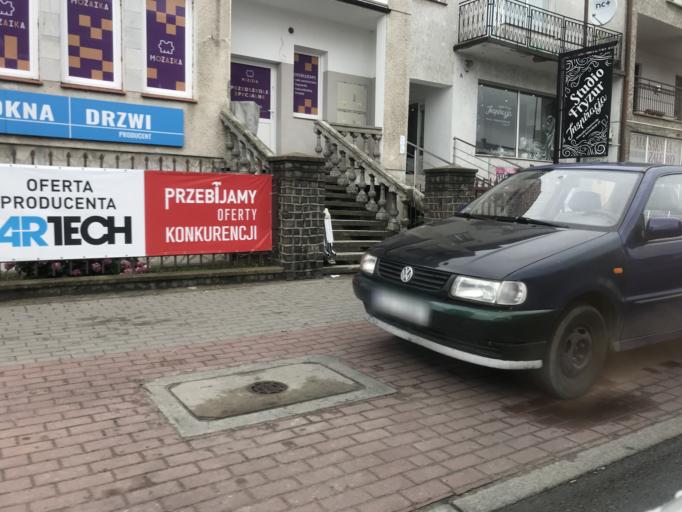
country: PL
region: Warmian-Masurian Voivodeship
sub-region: Powiat elblaski
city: Elblag
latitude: 54.1535
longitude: 19.4191
